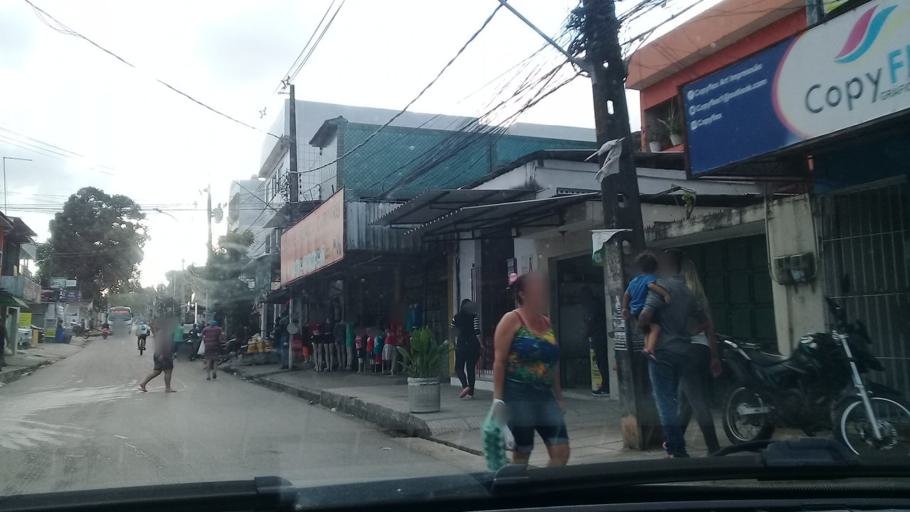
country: BR
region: Pernambuco
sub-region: Jaboatao Dos Guararapes
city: Jaboatao
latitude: -8.1369
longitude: -34.9375
